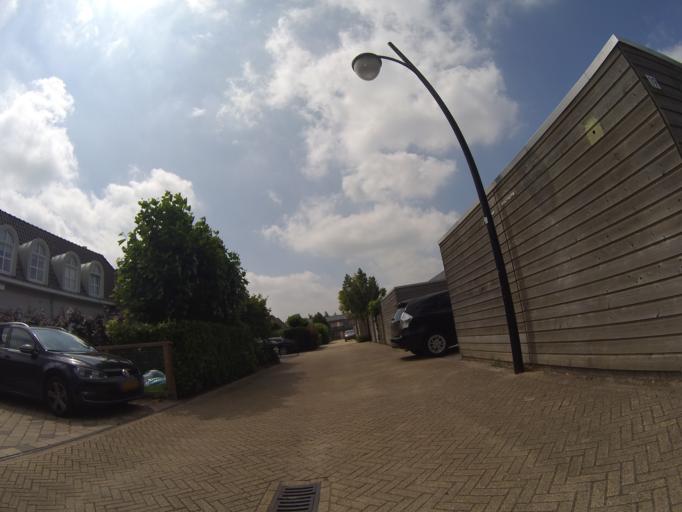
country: NL
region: Utrecht
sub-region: Gemeente Amersfoort
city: Hoogland
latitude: 52.2013
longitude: 5.4162
